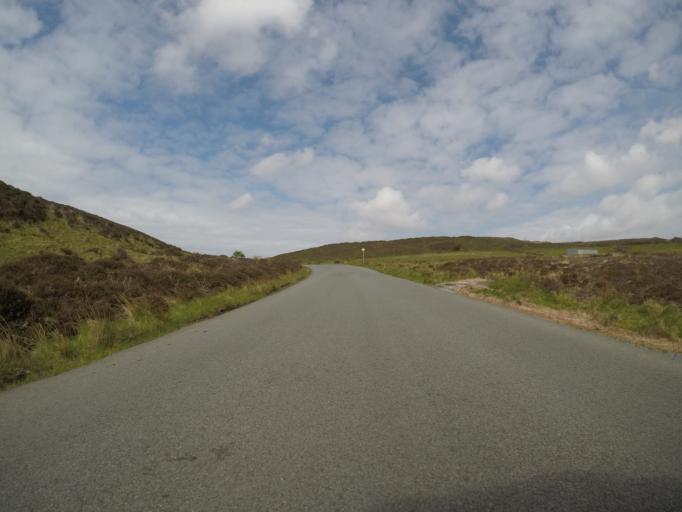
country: GB
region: Scotland
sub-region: Highland
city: Portree
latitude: 57.5937
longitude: -6.3733
